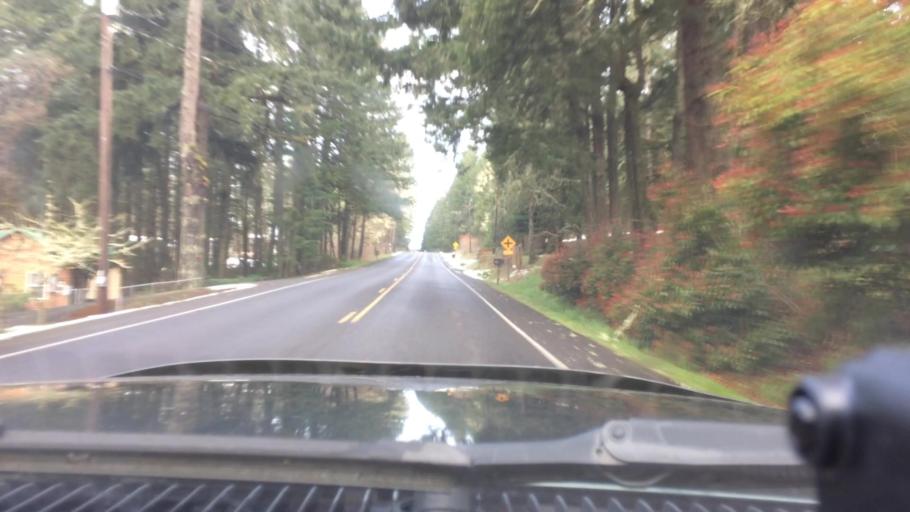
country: US
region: Oregon
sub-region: Lane County
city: Veneta
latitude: 44.1355
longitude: -123.3518
